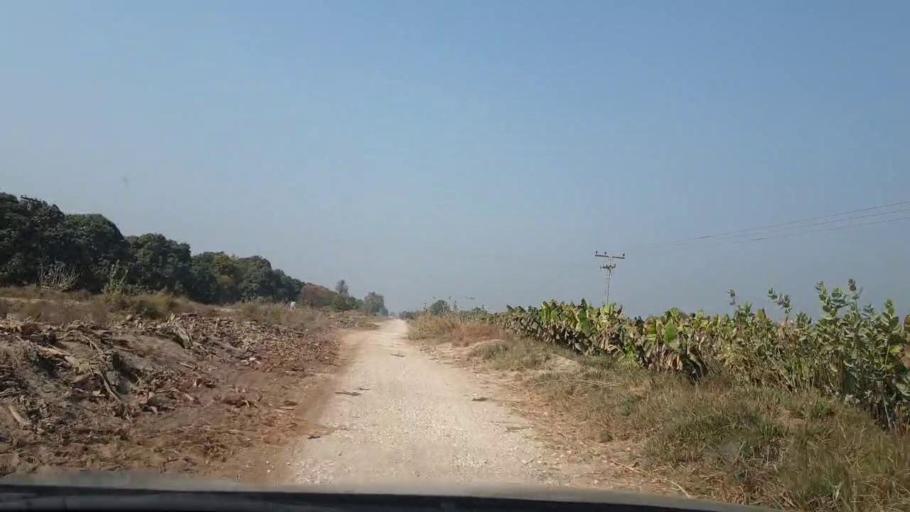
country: PK
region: Sindh
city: Tando Allahyar
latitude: 25.5260
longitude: 68.7536
